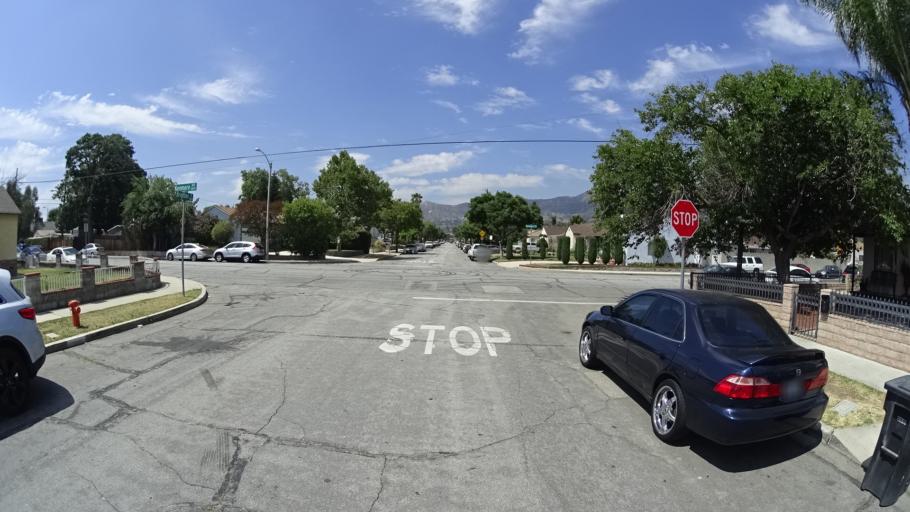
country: US
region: California
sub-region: Los Angeles County
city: Burbank
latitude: 34.1935
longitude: -118.3369
